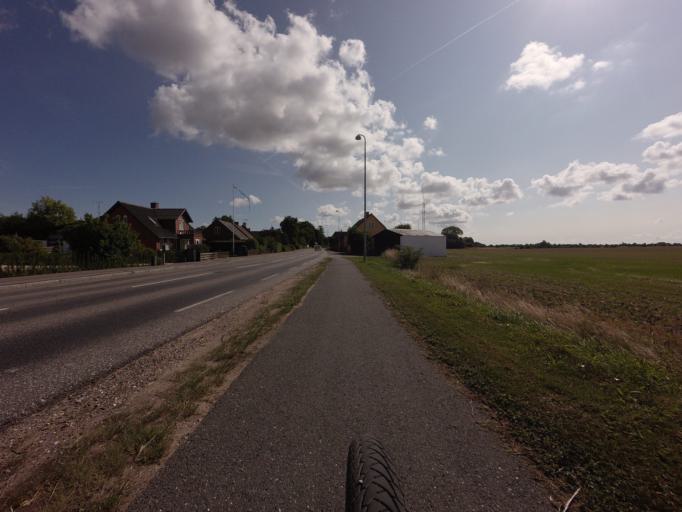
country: DK
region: Zealand
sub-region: Vordingborg Kommune
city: Stege
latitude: 54.9920
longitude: 12.3383
